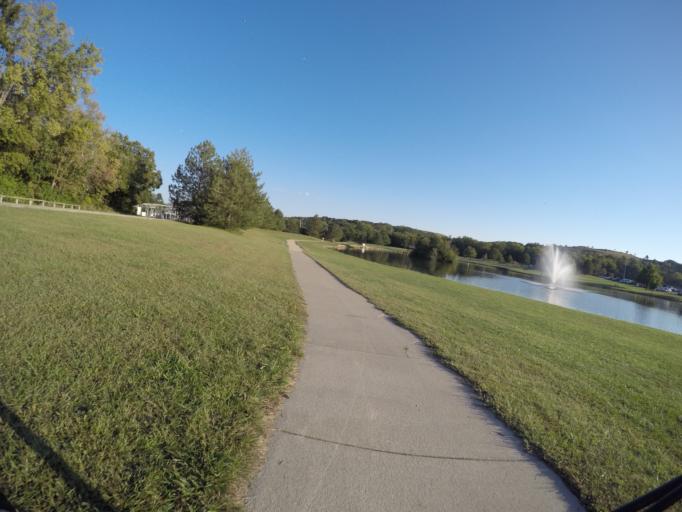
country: US
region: Kansas
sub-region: Riley County
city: Manhattan
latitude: 39.1850
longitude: -96.6300
